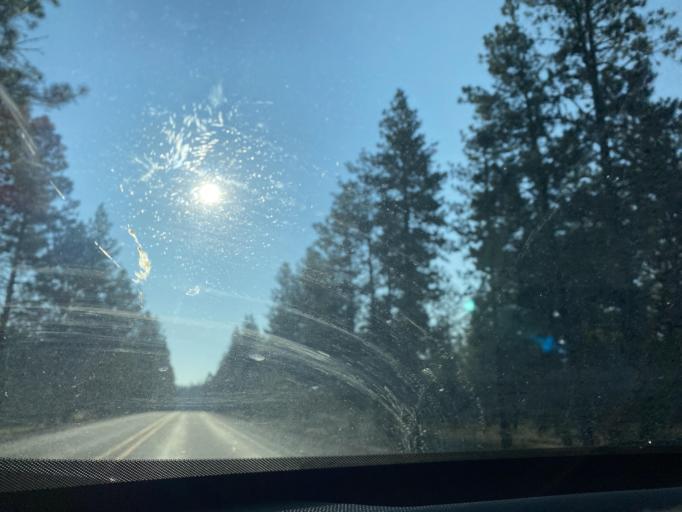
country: US
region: Oregon
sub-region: Deschutes County
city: Sunriver
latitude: 43.8694
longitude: -121.4207
